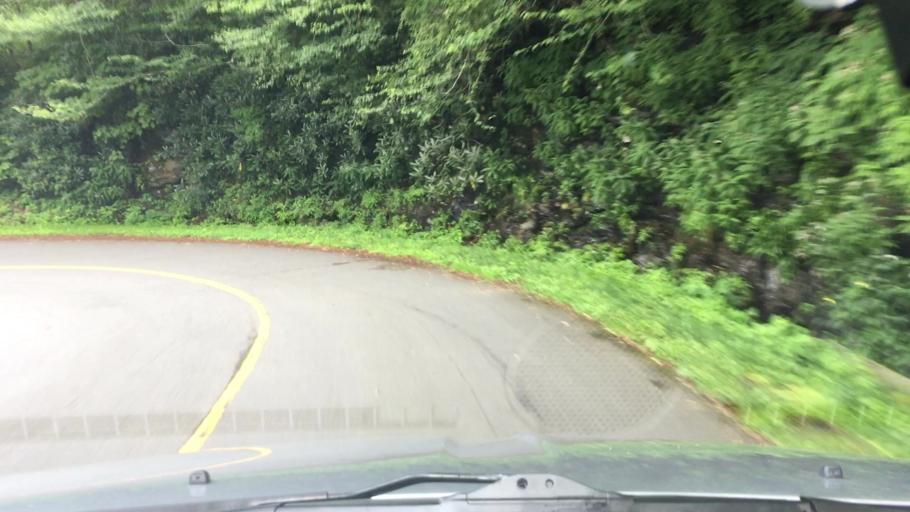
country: US
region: North Carolina
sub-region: Buncombe County
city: Swannanoa
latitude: 35.7018
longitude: -82.3899
